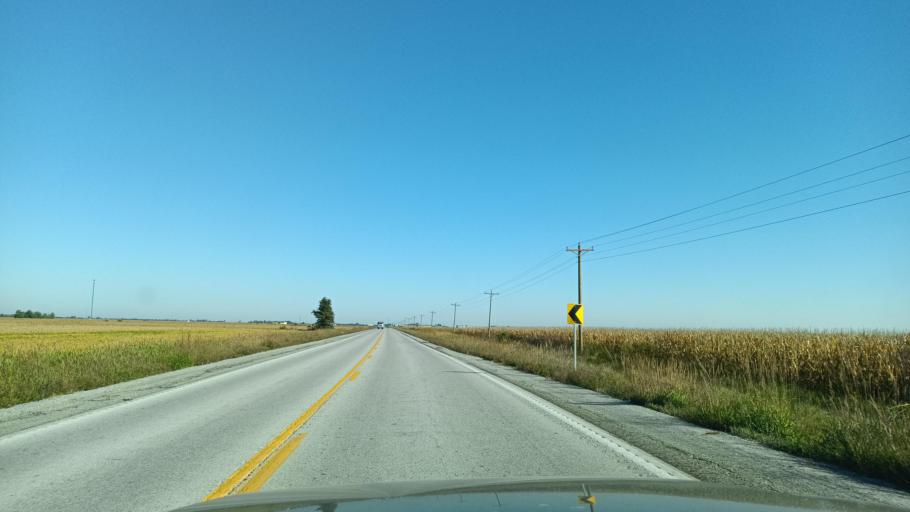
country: US
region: Missouri
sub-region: Audrain County
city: Vandalia
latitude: 39.4167
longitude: -91.6367
